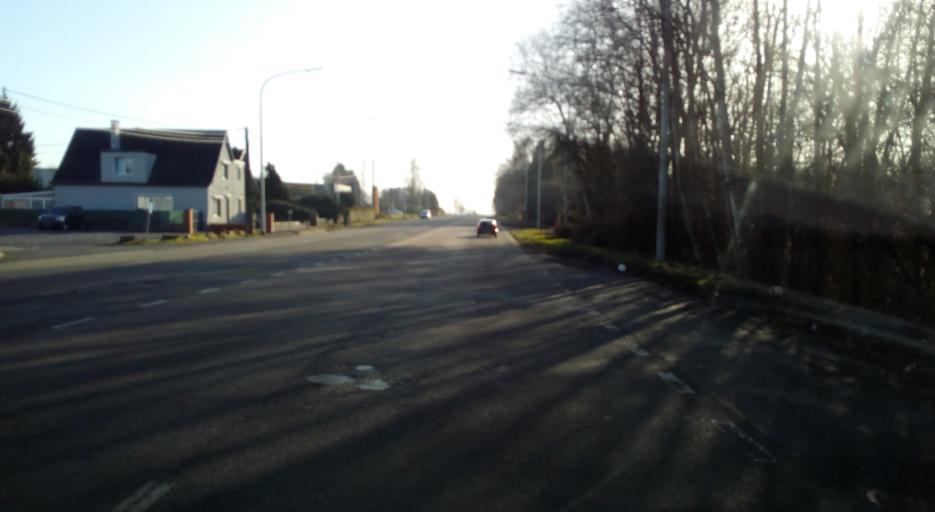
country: BE
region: Wallonia
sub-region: Province du Hainaut
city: Gerpinnes
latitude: 50.3027
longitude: 4.4814
